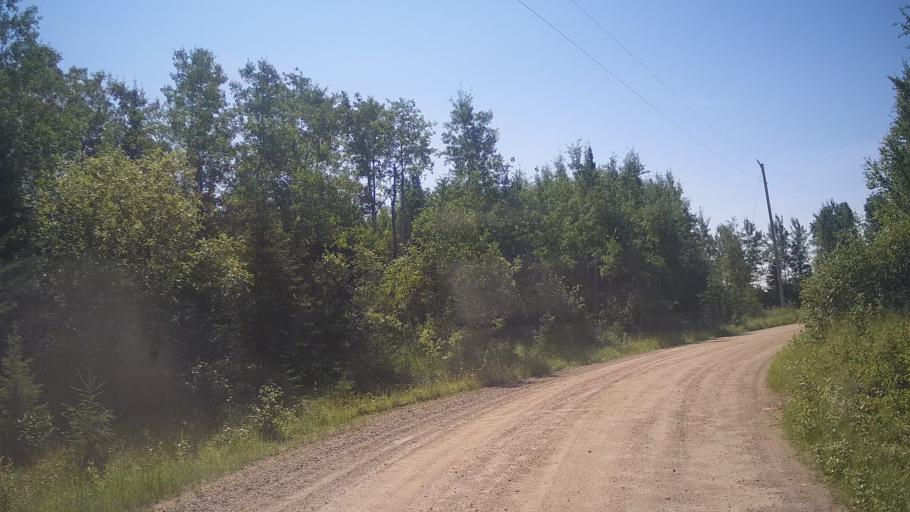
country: CA
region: Ontario
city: Dryden
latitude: 49.8160
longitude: -93.3288
